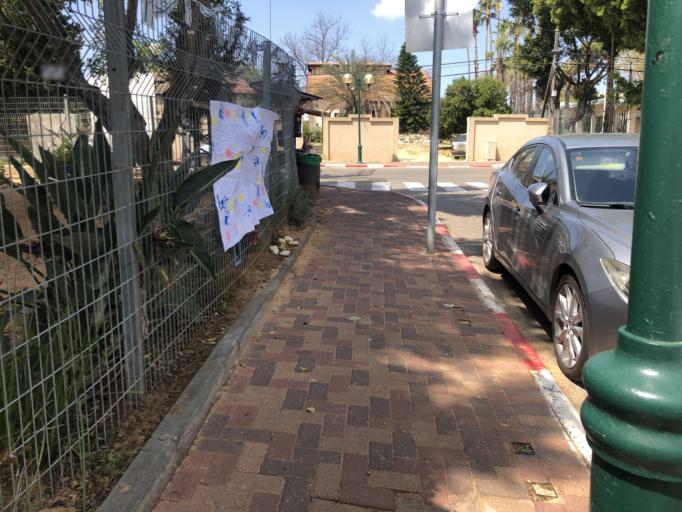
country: IL
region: Central District
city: Kfar Saba
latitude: 32.1555
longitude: 34.9149
